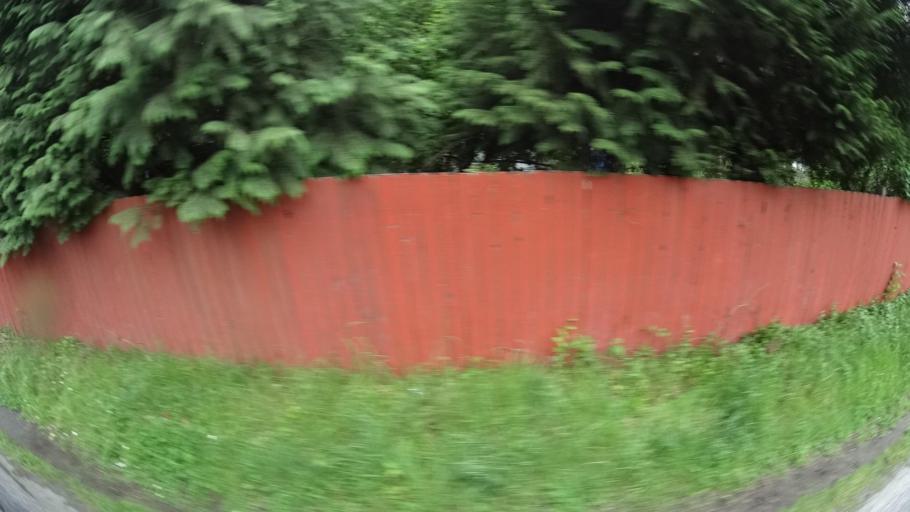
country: US
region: California
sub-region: Humboldt County
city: Willow Creek
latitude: 41.0511
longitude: -123.6680
